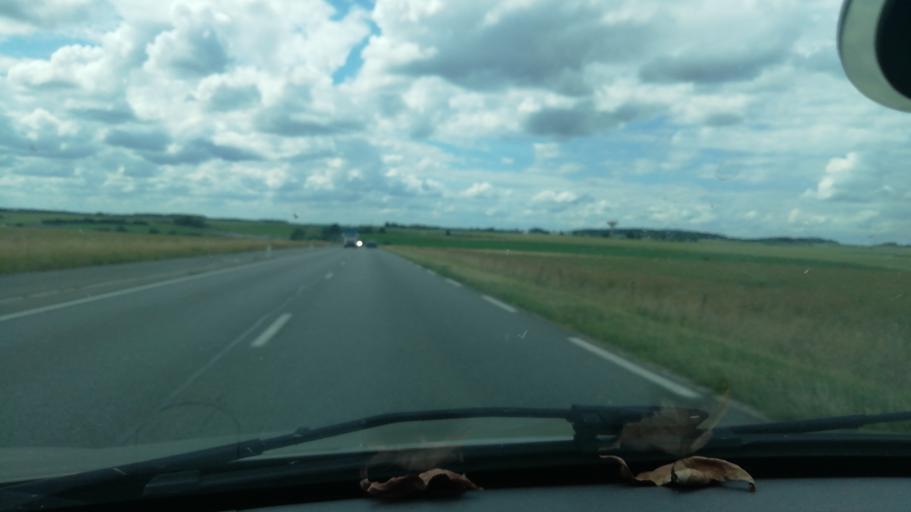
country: FR
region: Nord-Pas-de-Calais
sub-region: Departement du Pas-de-Calais
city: Anzin-Saint-Aubin
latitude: 50.3235
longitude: 2.7434
